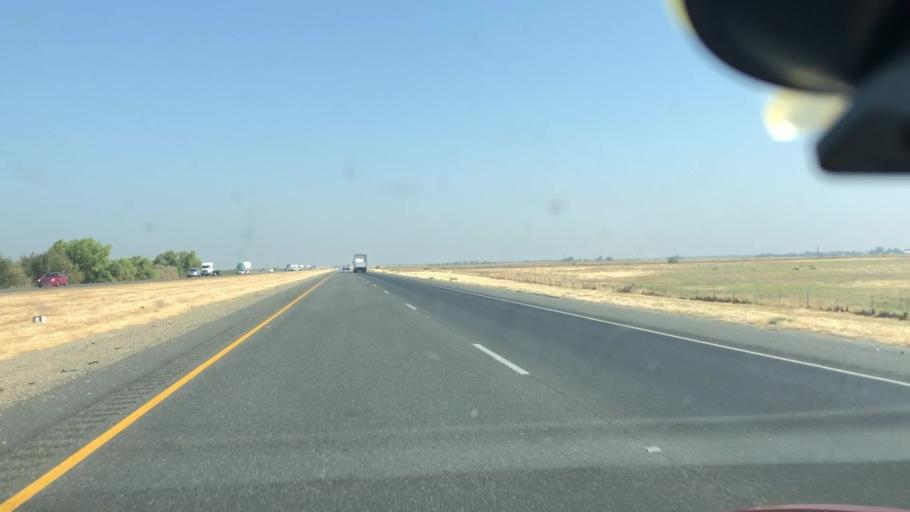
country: US
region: California
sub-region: Sacramento County
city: Laguna
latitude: 38.3464
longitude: -121.4706
